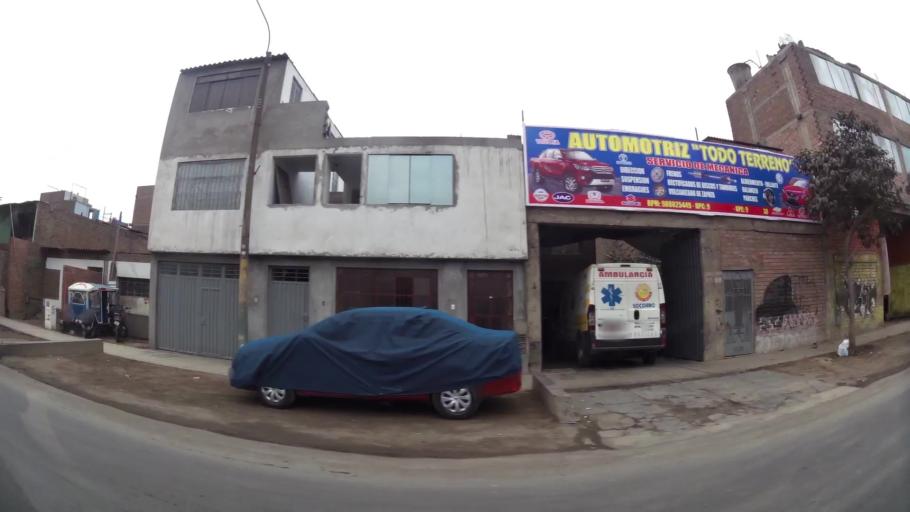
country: PE
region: Lima
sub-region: Lima
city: Vitarte
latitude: -12.0423
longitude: -76.9664
